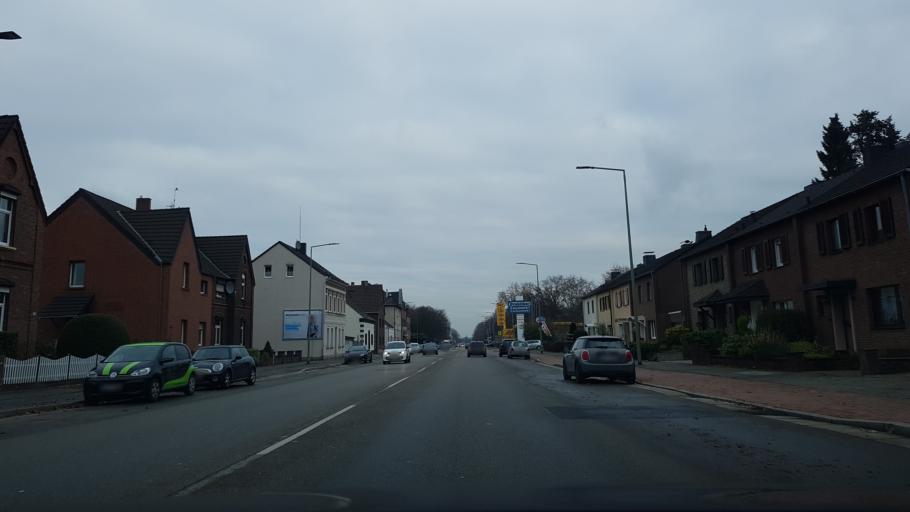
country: DE
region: North Rhine-Westphalia
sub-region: Regierungsbezirk Dusseldorf
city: Moers
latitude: 51.4439
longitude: 6.6842
